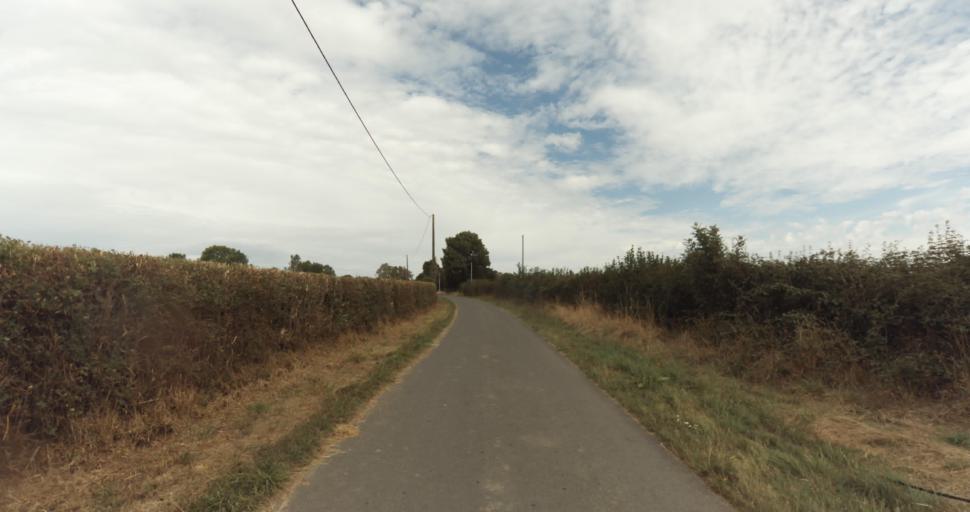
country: FR
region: Lower Normandy
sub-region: Departement du Calvados
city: Orbec
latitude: 48.9643
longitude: 0.3825
